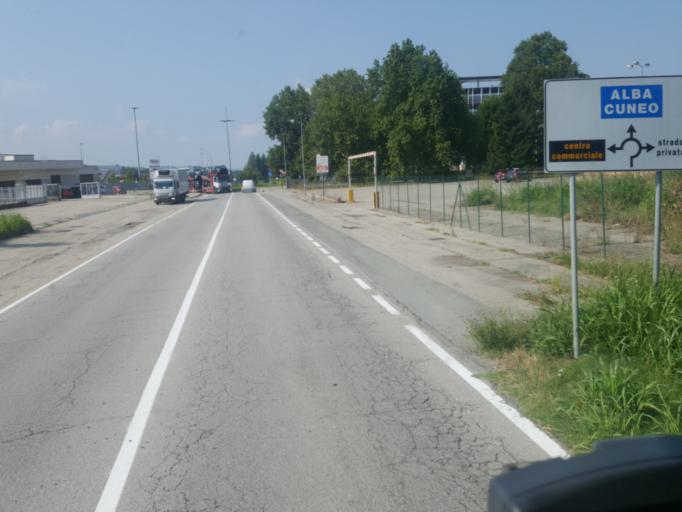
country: IT
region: Piedmont
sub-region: Provincia di Cuneo
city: Mussotto
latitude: 44.7195
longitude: 8.0360
